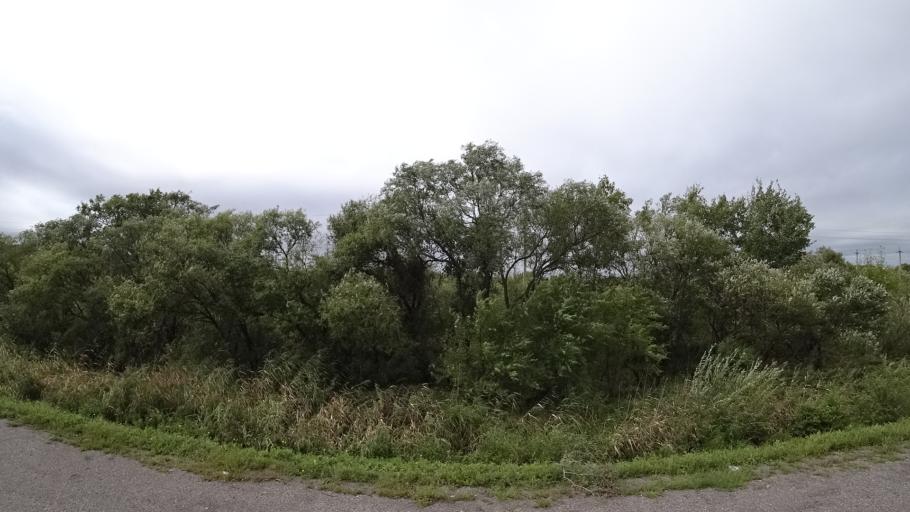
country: RU
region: Primorskiy
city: Monastyrishche
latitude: 44.1735
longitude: 132.4412
